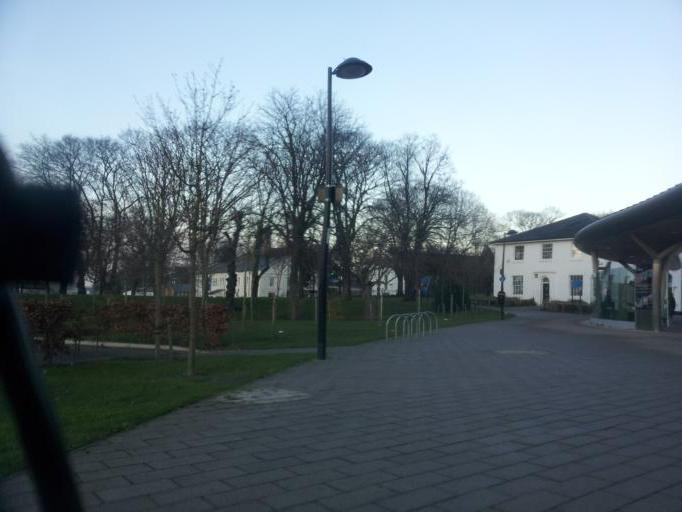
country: GB
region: England
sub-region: Kent
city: Chatham
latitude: 51.3849
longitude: 0.5239
